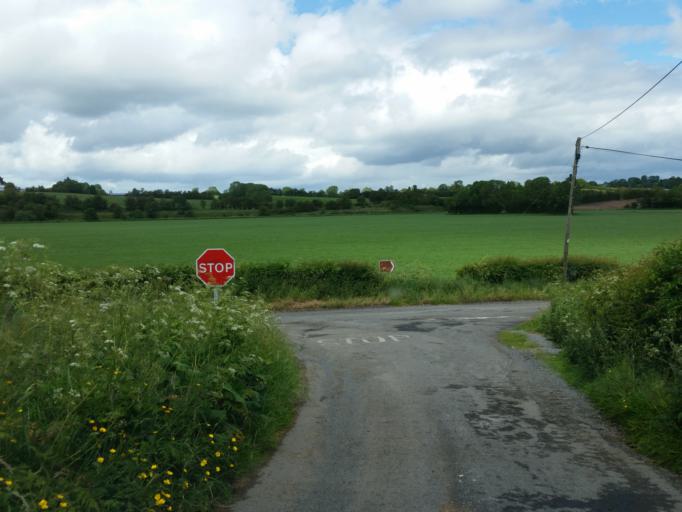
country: GB
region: Northern Ireland
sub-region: Omagh District
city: Omagh
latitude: 54.5479
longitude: -7.1359
